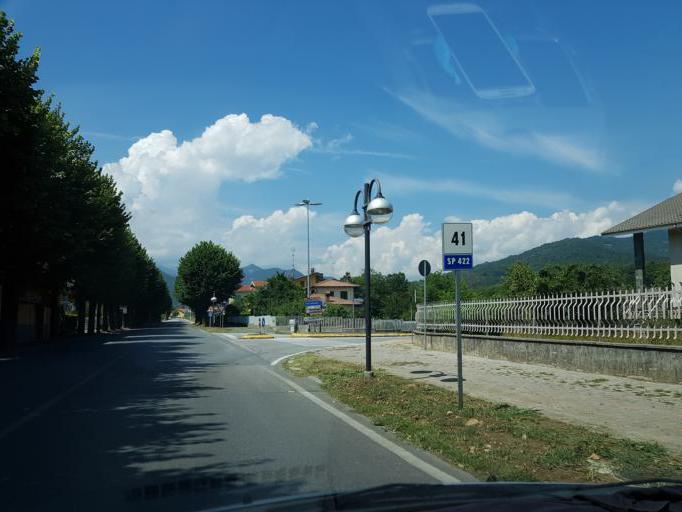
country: IT
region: Piedmont
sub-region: Provincia di Cuneo
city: Tettorosso
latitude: 44.4672
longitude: 7.3495
